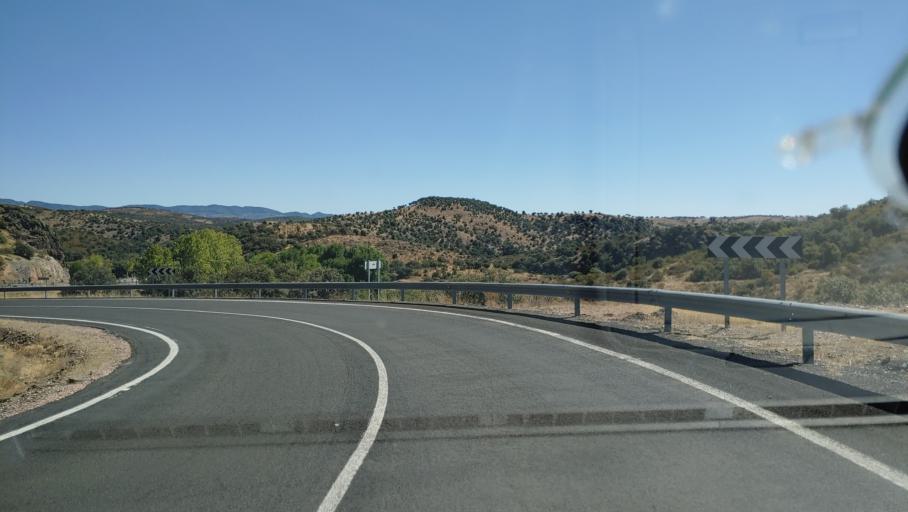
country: ES
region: Andalusia
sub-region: Provincia de Jaen
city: Genave
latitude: 38.5170
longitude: -2.7874
